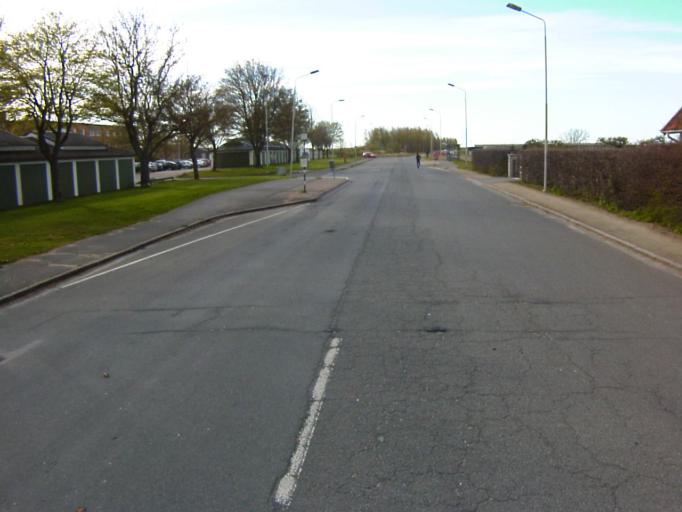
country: SE
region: Skane
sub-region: Kristianstads Kommun
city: Kristianstad
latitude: 56.0619
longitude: 14.1593
